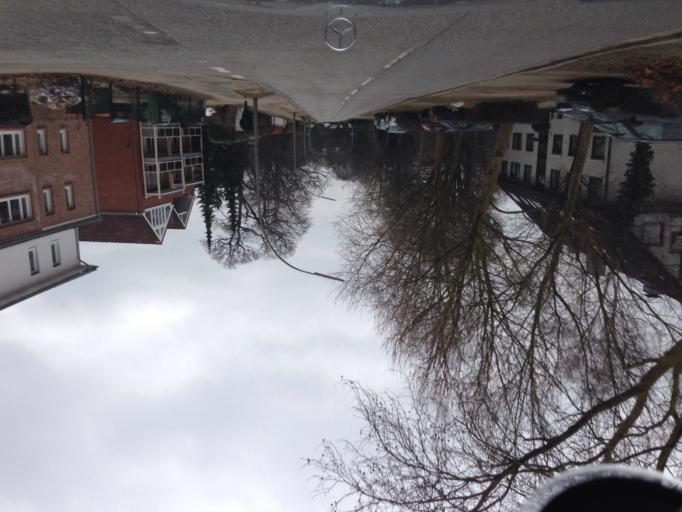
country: DE
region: Hamburg
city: Steilshoop
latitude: 53.6157
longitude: 10.0722
